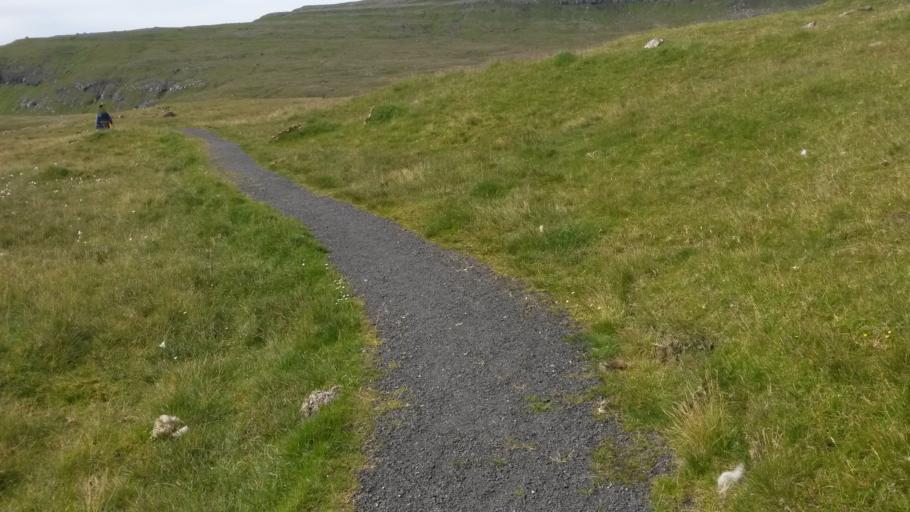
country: FO
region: Streymoy
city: Argir
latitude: 61.9915
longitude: -6.8493
